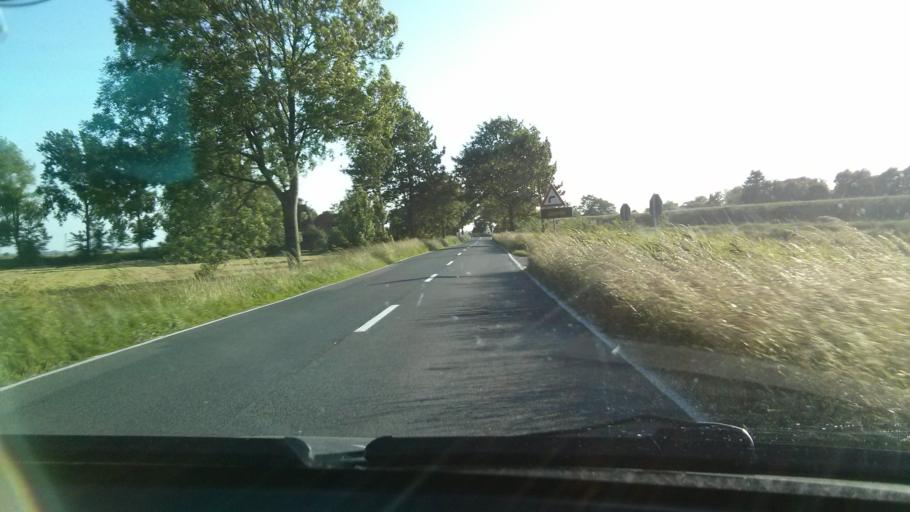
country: DE
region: Bremen
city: Bremerhaven
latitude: 53.4788
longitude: 8.5772
